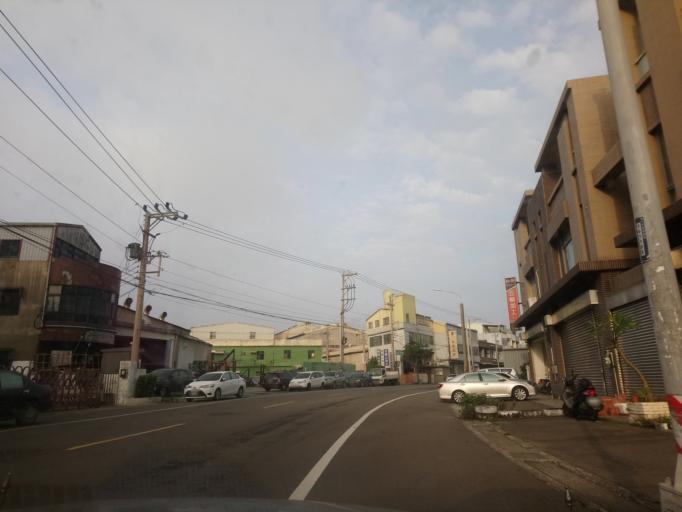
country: TW
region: Taiwan
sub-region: Hsinchu
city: Hsinchu
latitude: 24.7949
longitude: 120.9327
